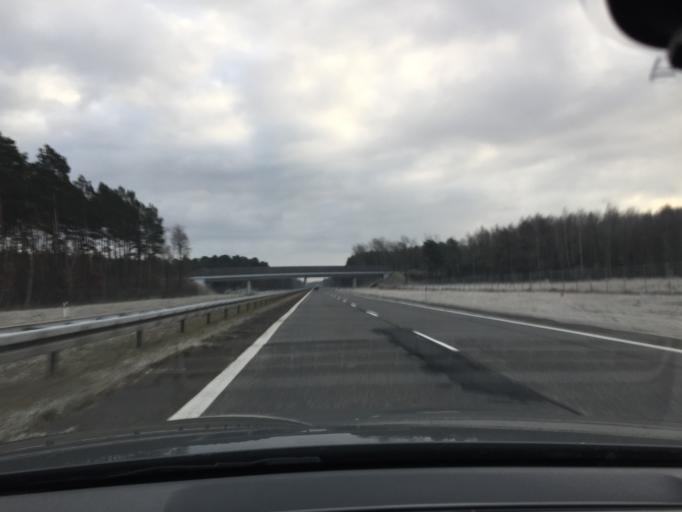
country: PL
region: Lubusz
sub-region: Powiat zarski
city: Trzebiel
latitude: 51.6222
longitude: 14.8964
